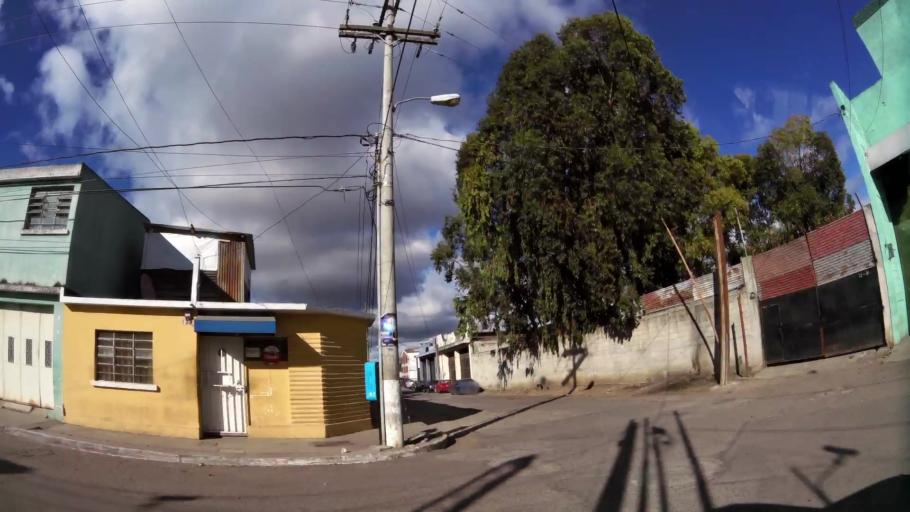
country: GT
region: Guatemala
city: Guatemala City
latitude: 14.6340
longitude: -90.5009
